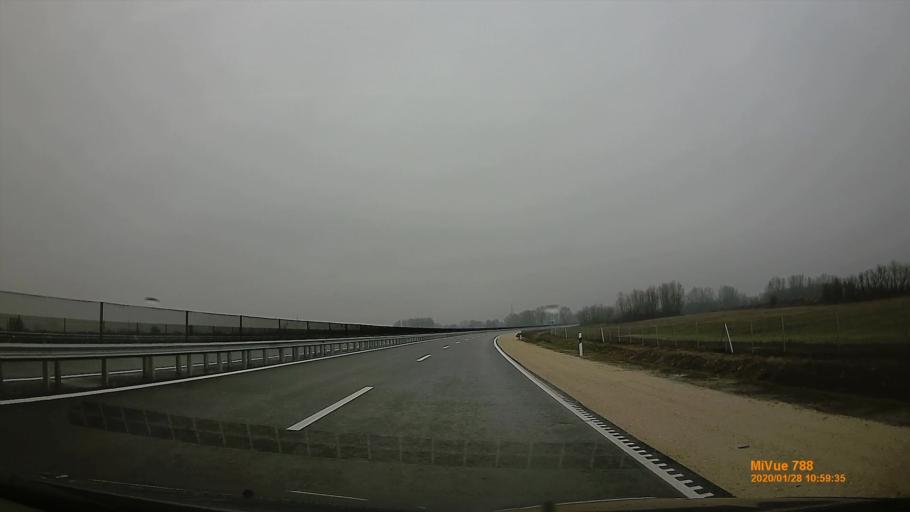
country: HU
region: Pest
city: Ullo
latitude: 47.3828
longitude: 19.3809
